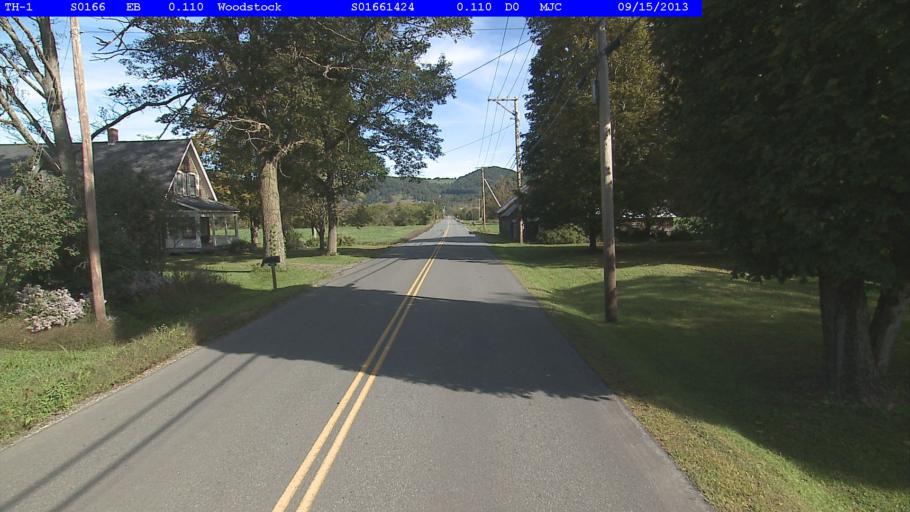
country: US
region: Vermont
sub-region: Windsor County
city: Woodstock
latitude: 43.6399
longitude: -72.5253
